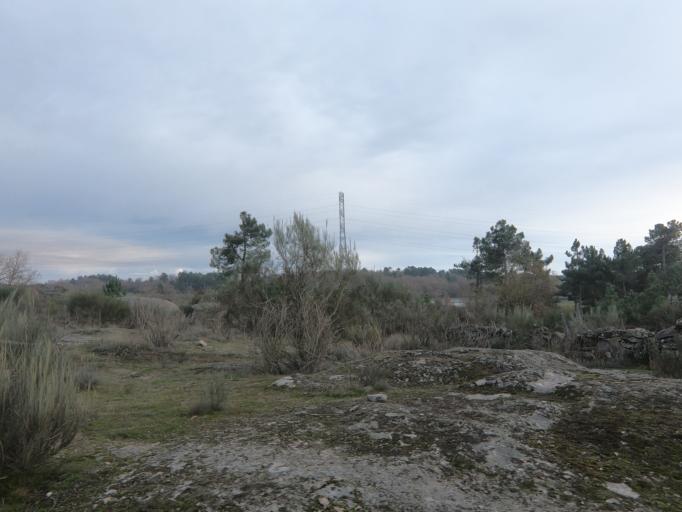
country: PT
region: Vila Real
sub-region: Sabrosa
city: Sabrosa
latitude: 41.3196
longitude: -7.6292
